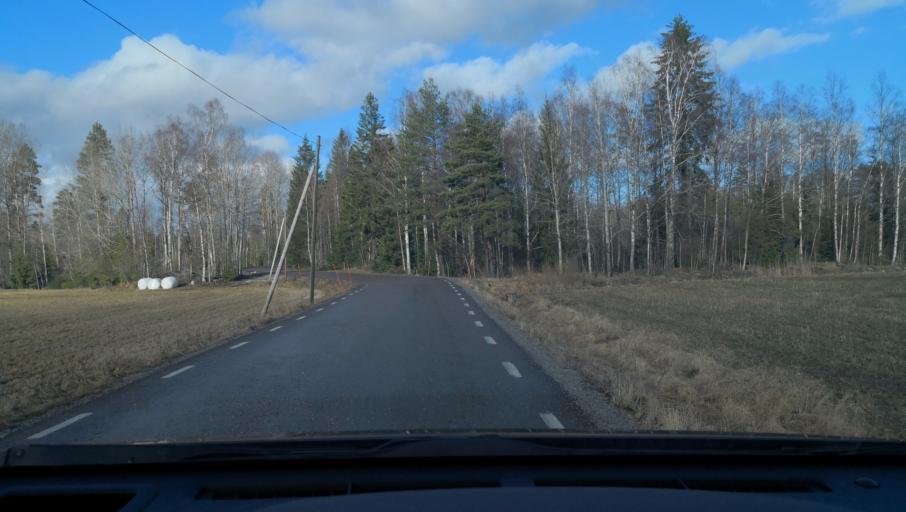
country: SE
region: Vaestmanland
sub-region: Arboga Kommun
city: Arboga
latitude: 59.3537
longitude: 15.8375
